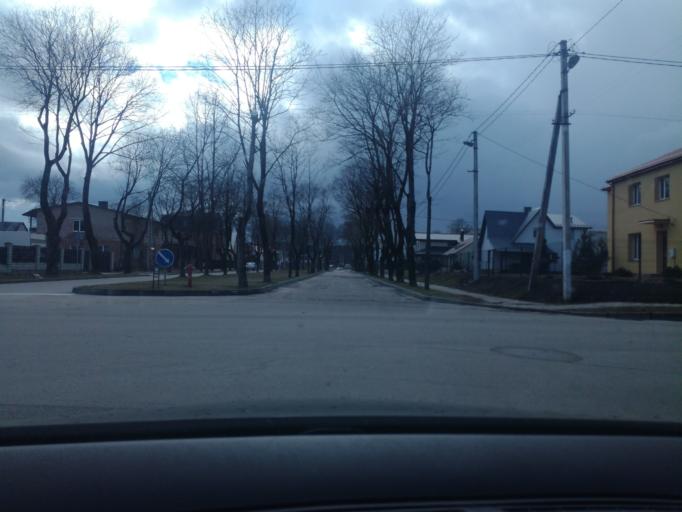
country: LT
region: Alytaus apskritis
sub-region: Alytus
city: Alytus
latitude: 54.3909
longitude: 24.0480
